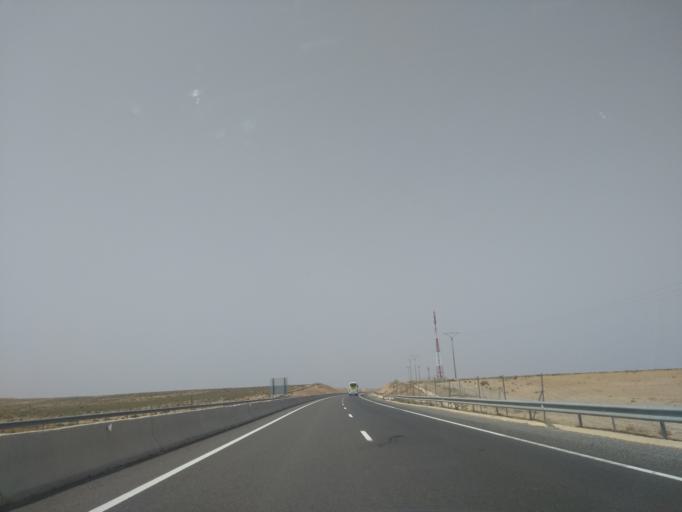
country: MA
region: Marrakech-Tensift-Al Haouz
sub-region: Chichaoua
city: Chichaoua
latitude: 31.5612
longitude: -8.4331
